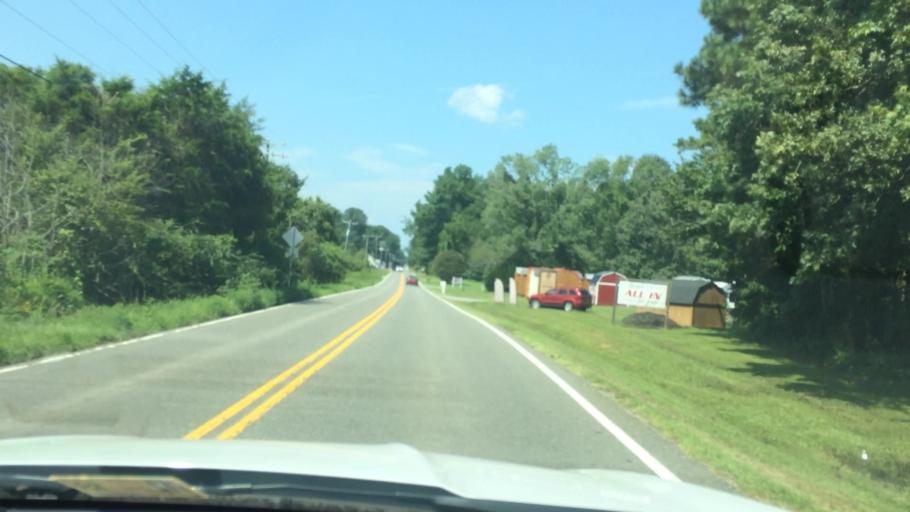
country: US
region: Virginia
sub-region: New Kent County
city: New Kent
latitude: 37.5336
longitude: -77.1190
